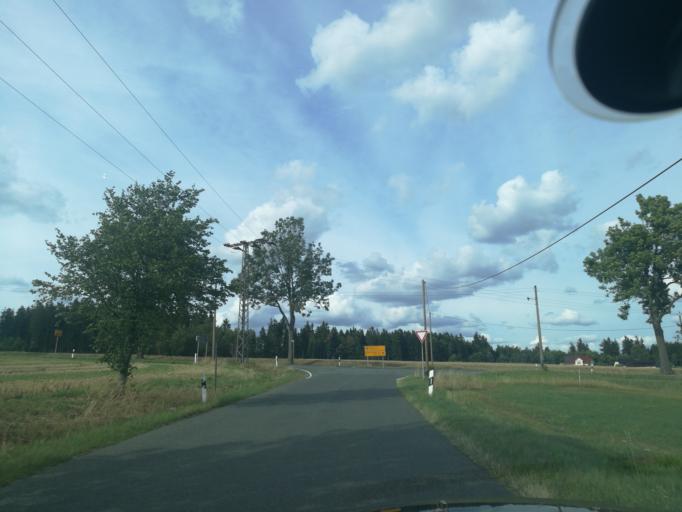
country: DE
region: Saxony
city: Triebel
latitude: 50.3320
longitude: 12.1207
